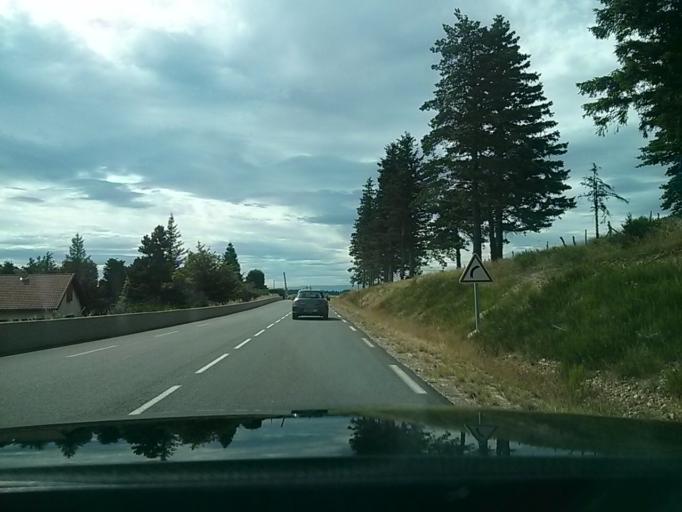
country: FR
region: Rhone-Alpes
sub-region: Departement de la Loire
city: Saint-Genest-Malifaux
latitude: 45.3731
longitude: 4.4981
